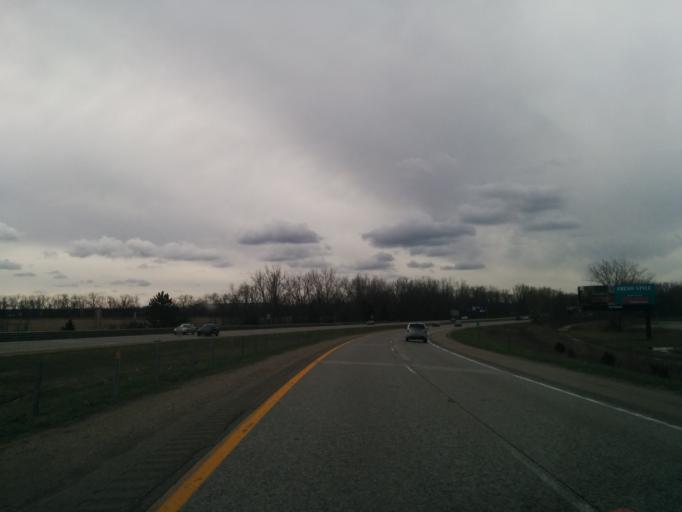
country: US
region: Michigan
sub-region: Kent County
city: Grand Rapids
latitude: 42.9543
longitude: -85.7054
